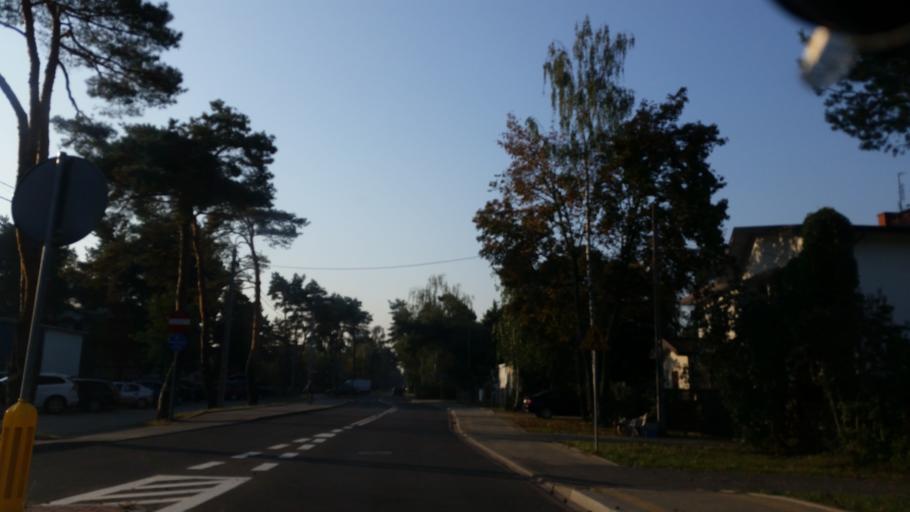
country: PL
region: Masovian Voivodeship
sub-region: Powiat otwocki
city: Jozefow
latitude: 52.1449
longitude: 21.2144
